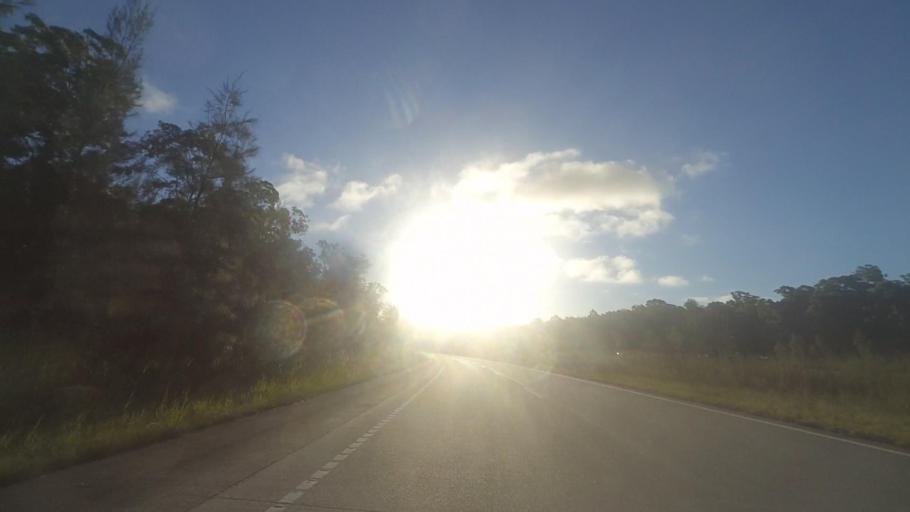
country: AU
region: New South Wales
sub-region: Great Lakes
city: Hawks Nest
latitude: -32.5481
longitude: 152.1562
